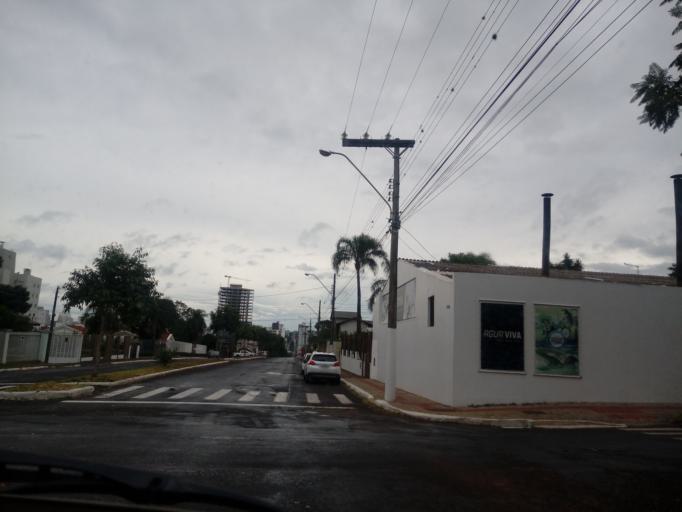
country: BR
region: Santa Catarina
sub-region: Chapeco
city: Chapeco
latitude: -27.1083
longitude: -52.6213
